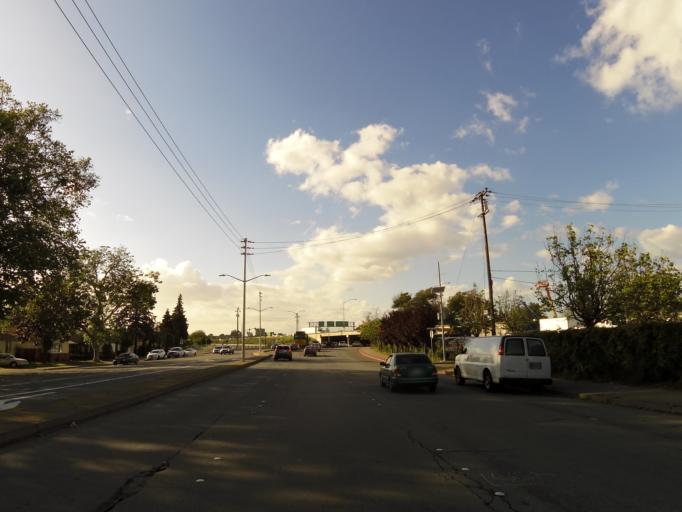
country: US
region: California
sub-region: Alameda County
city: San Lorenzo
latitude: 37.6833
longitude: -122.1292
